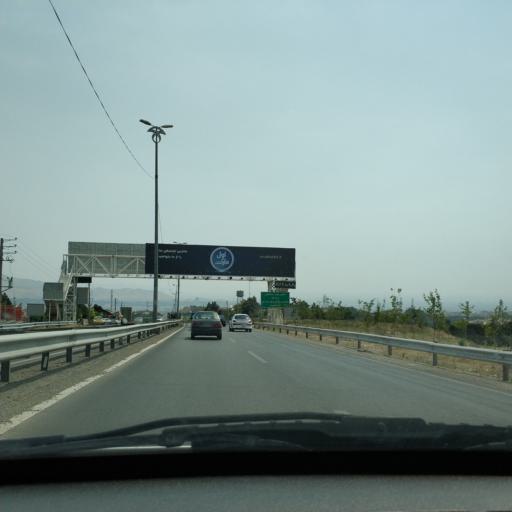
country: IR
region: Tehran
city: Tajrish
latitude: 35.7774
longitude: 51.5612
